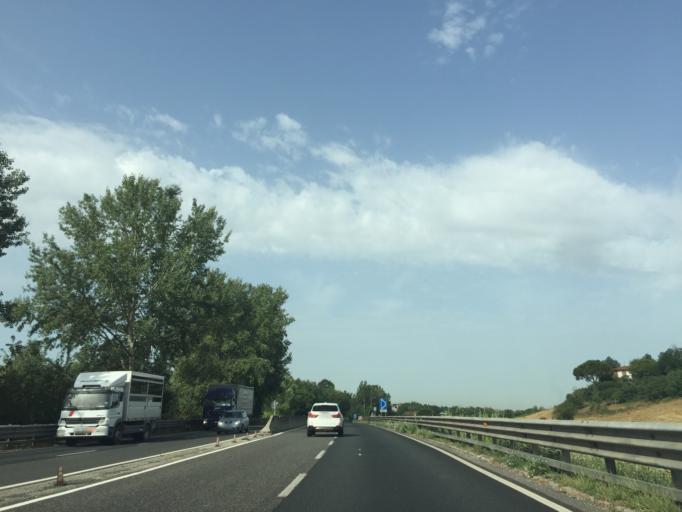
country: IT
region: Tuscany
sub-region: Province of Pisa
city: San Romano
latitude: 43.6860
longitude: 10.7739
